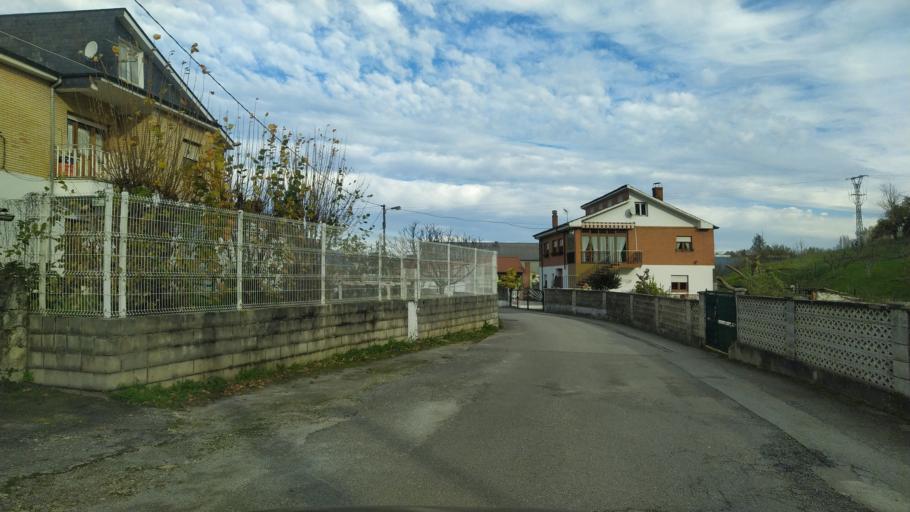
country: ES
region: Cantabria
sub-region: Provincia de Cantabria
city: Reocin
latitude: 43.3558
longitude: -4.0881
